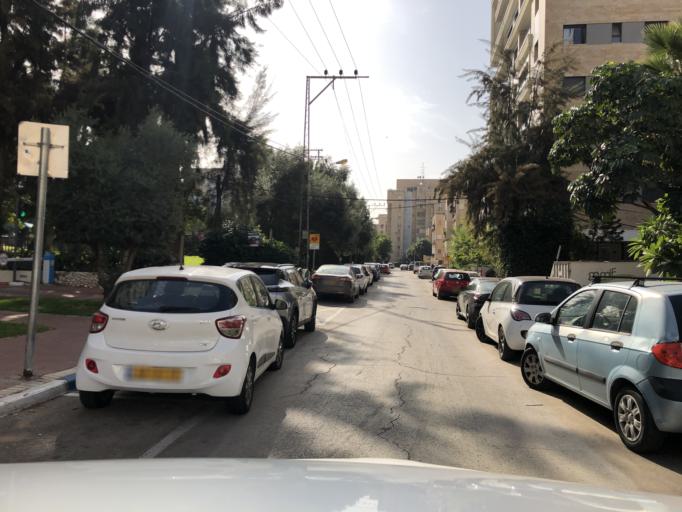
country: IL
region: Tel Aviv
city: Bene Beraq
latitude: 32.0689
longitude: 34.8307
